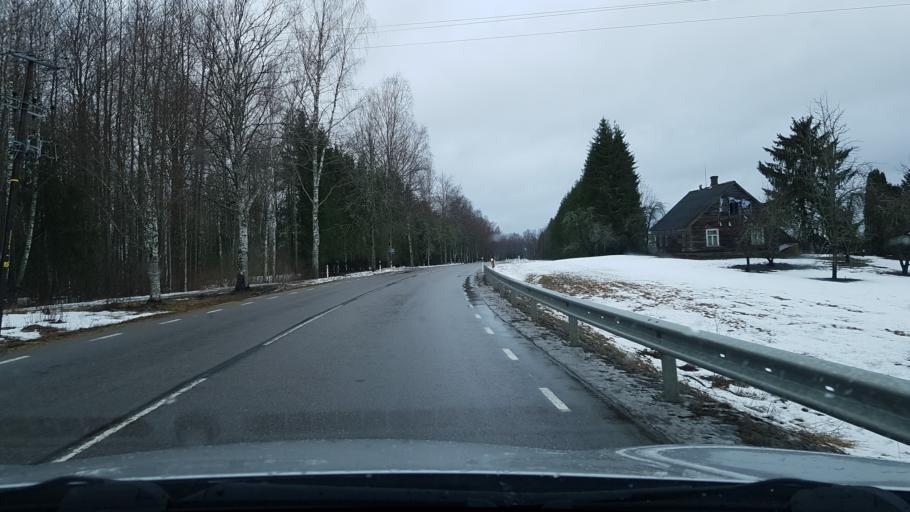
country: LV
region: Apes Novads
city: Ape
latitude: 57.6000
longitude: 26.6128
